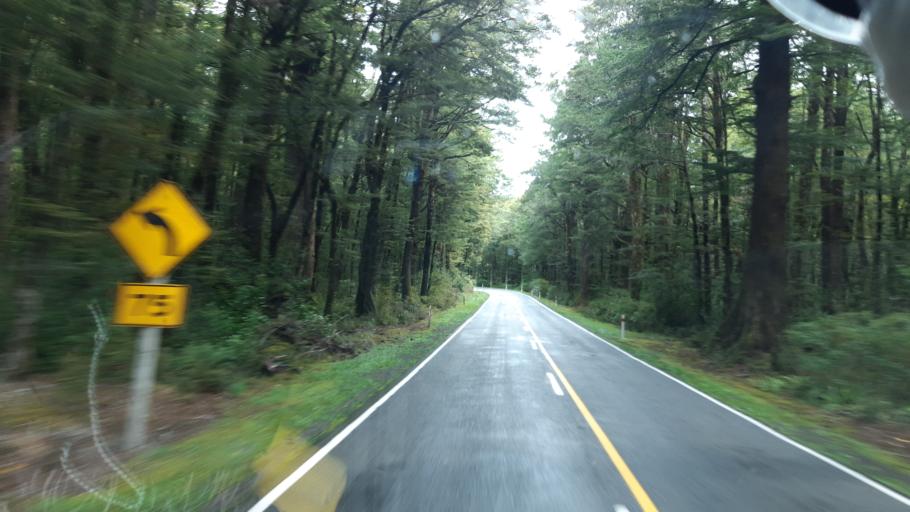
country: NZ
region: Canterbury
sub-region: Hurunui District
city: Amberley
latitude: -42.3807
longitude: 172.3072
